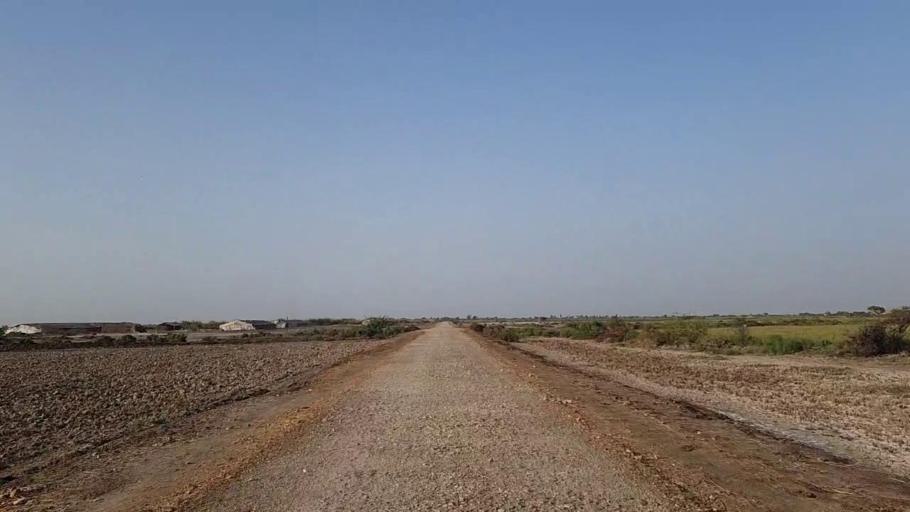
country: PK
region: Sindh
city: Jati
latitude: 24.3685
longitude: 68.1455
